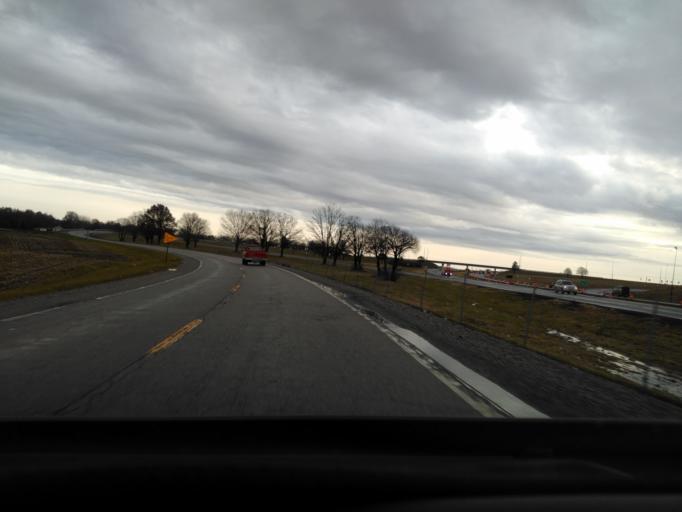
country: US
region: Illinois
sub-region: Bond County
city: Greenville
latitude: 38.8522
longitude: -89.4578
